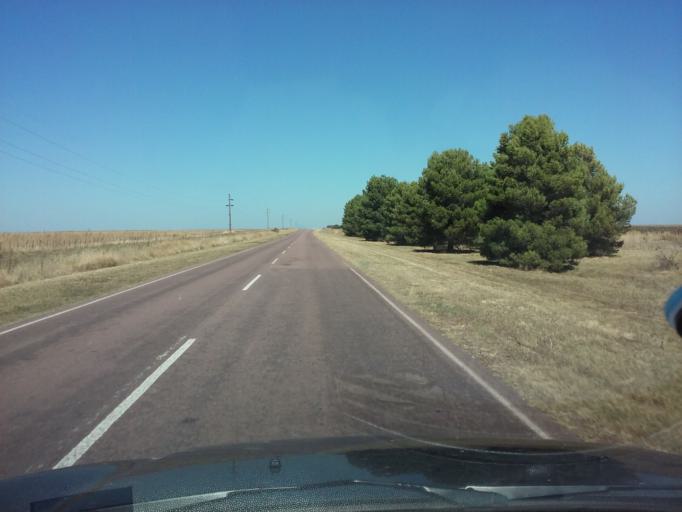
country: AR
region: La Pampa
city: Colonia Baron
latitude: -36.2464
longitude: -63.9428
